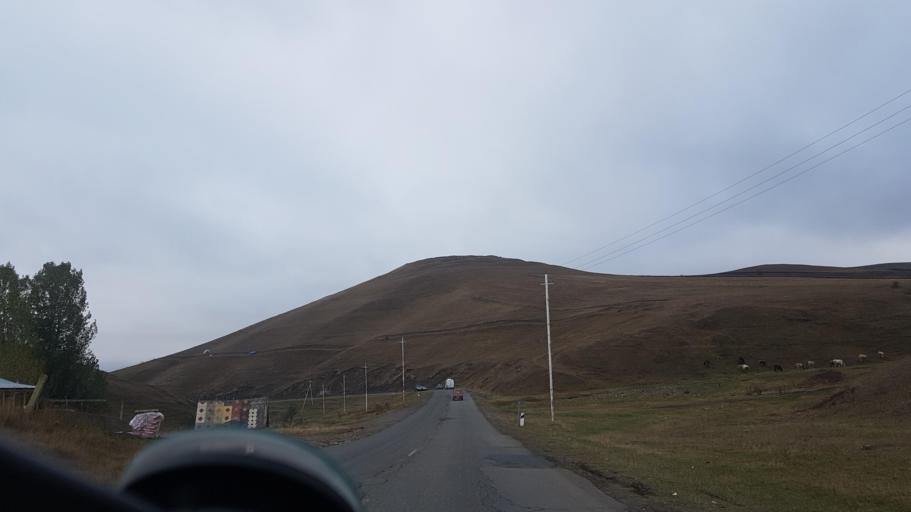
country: AZ
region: Gadabay Rayon
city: Ariqdam
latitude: 40.6187
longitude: 45.8118
